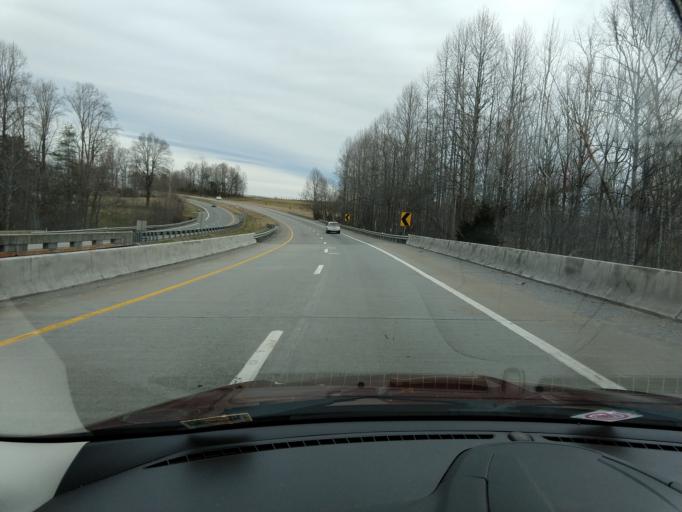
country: US
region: Virginia
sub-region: Franklin County
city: Henry Fork
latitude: 36.8625
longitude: -79.8712
